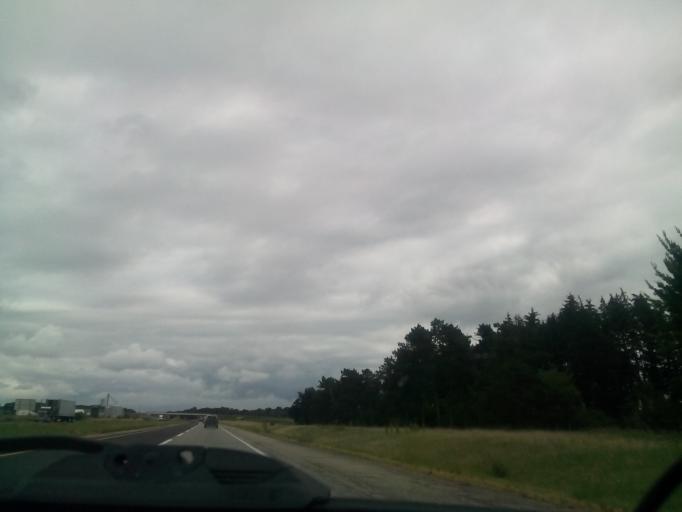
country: US
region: Michigan
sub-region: Saint Joseph County
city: Sturgis
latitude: 41.7446
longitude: -85.3242
